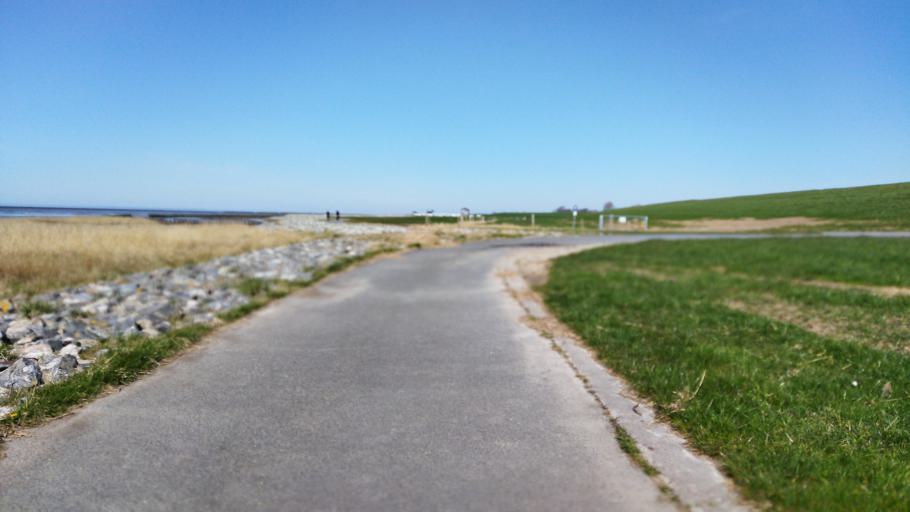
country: DE
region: Lower Saxony
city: Wremen
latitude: 53.6317
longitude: 8.5031
